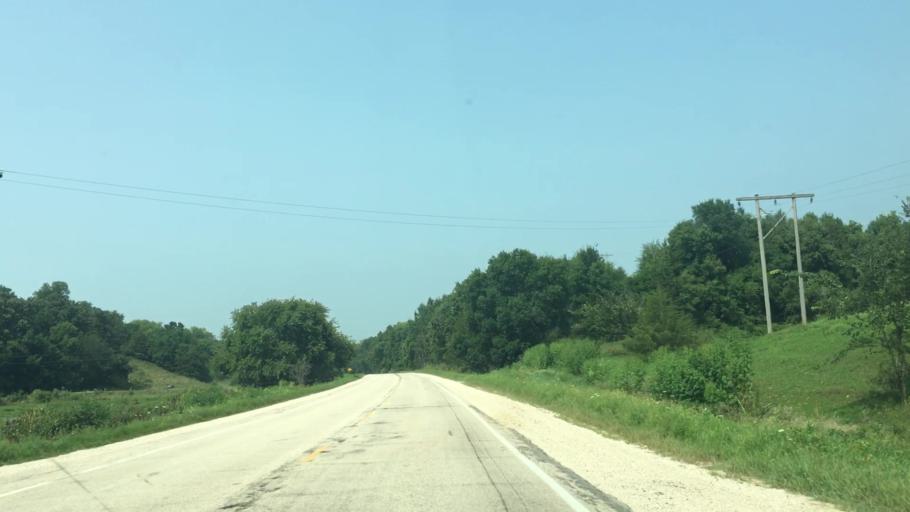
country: US
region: Iowa
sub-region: Fayette County
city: West Union
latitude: 43.0718
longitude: -91.8388
